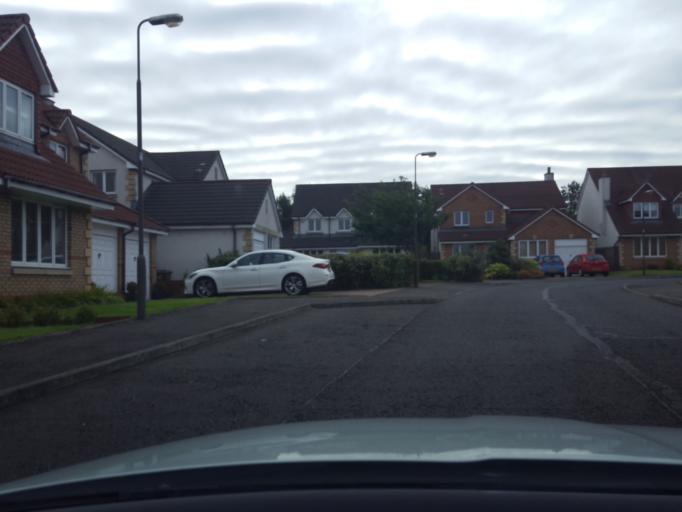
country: GB
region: Scotland
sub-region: West Lothian
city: Livingston
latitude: 55.8717
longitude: -3.5270
